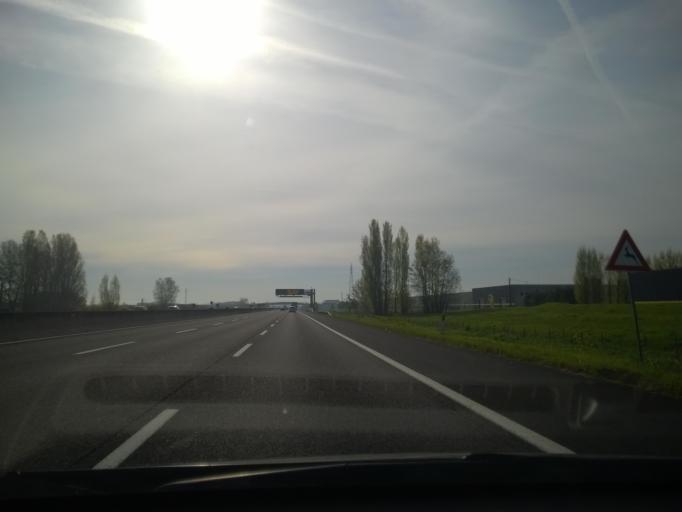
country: IT
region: Emilia-Romagna
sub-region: Provincia di Ravenna
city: Faenza
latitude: 44.3311
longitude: 11.8864
